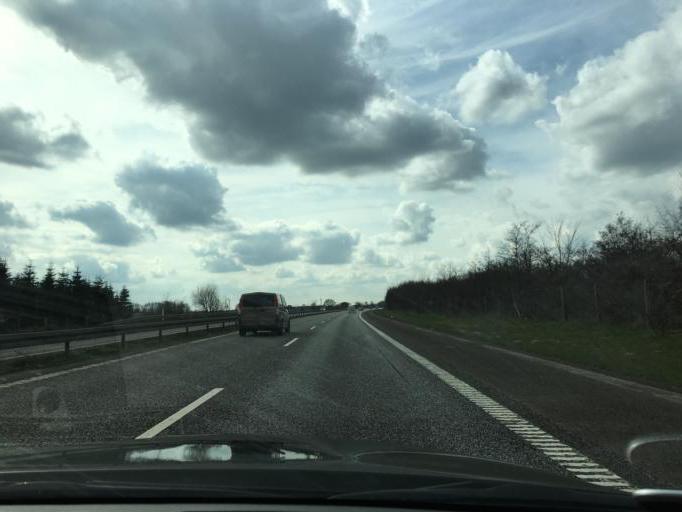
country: DK
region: South Denmark
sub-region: Kolding Kommune
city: Lunderskov
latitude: 55.4987
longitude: 9.2332
